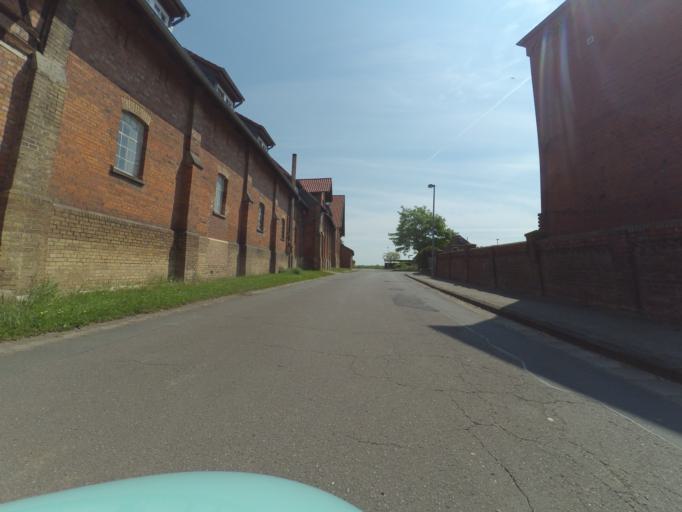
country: DE
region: Lower Saxony
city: Algermissen
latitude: 52.2704
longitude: 10.0141
